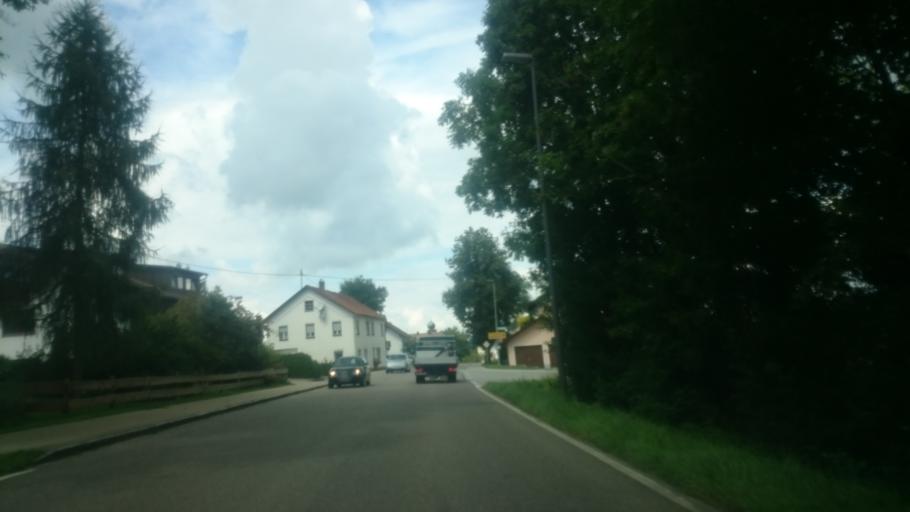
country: DE
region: Bavaria
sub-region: Swabia
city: Gunzach
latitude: 47.8202
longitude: 10.4405
